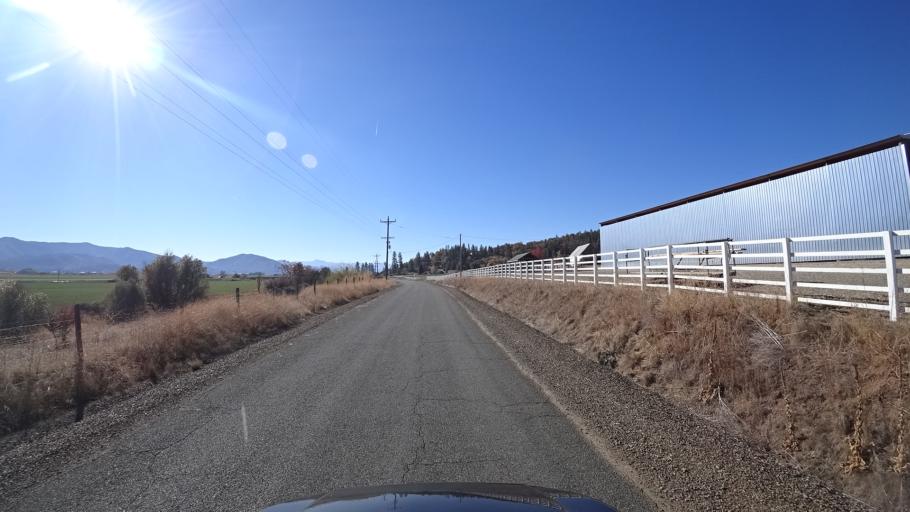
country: US
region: California
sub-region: Siskiyou County
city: Yreka
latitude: 41.5947
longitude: -122.8584
